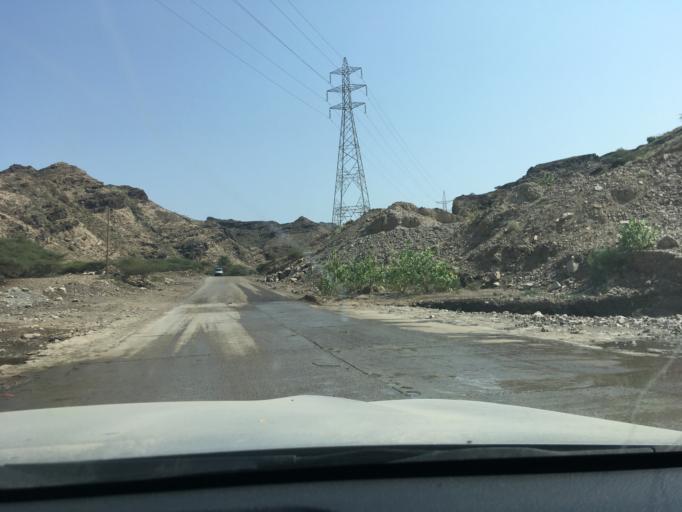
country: YE
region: Lahij
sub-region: Al Milah
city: Al Milah
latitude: 13.3551
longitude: 44.7688
